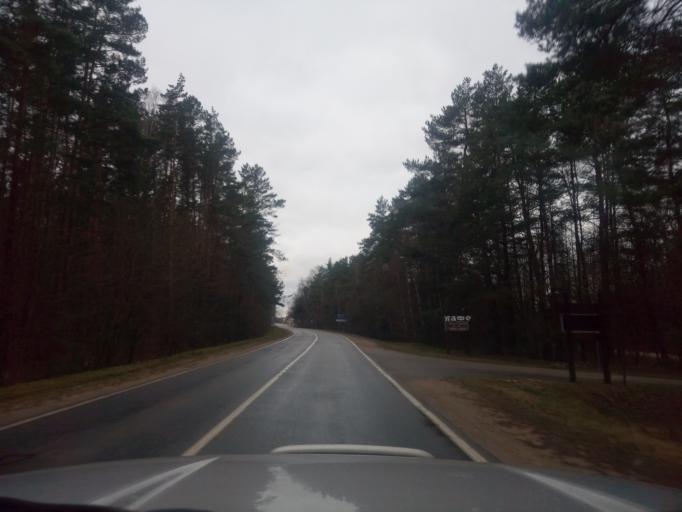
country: BY
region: Minsk
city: Kapyl'
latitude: 53.1589
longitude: 27.1084
